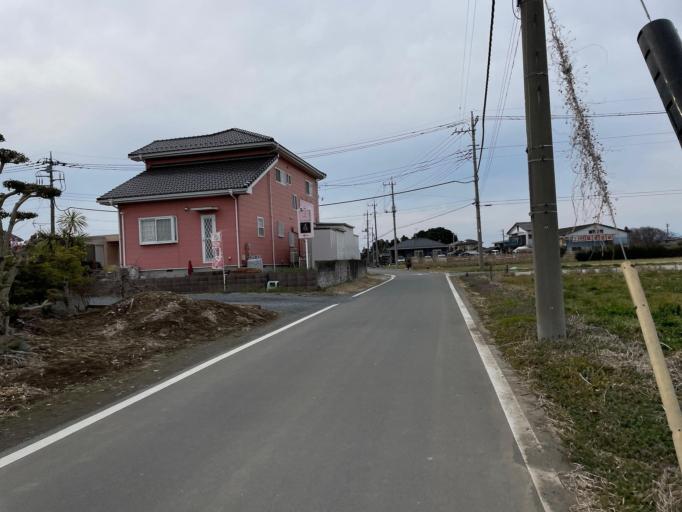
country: JP
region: Saitama
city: Kodamacho-kodamaminami
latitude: 36.2081
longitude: 139.1167
